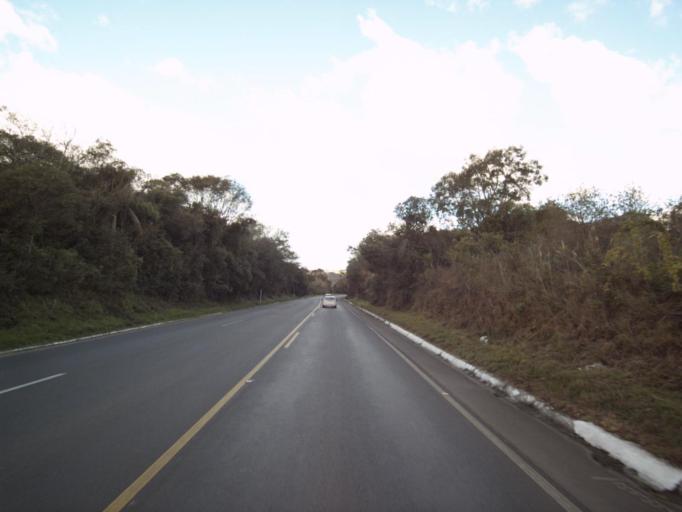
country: BR
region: Santa Catarina
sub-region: Campos Novos
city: Campos Novos
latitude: -27.3084
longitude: -51.3762
